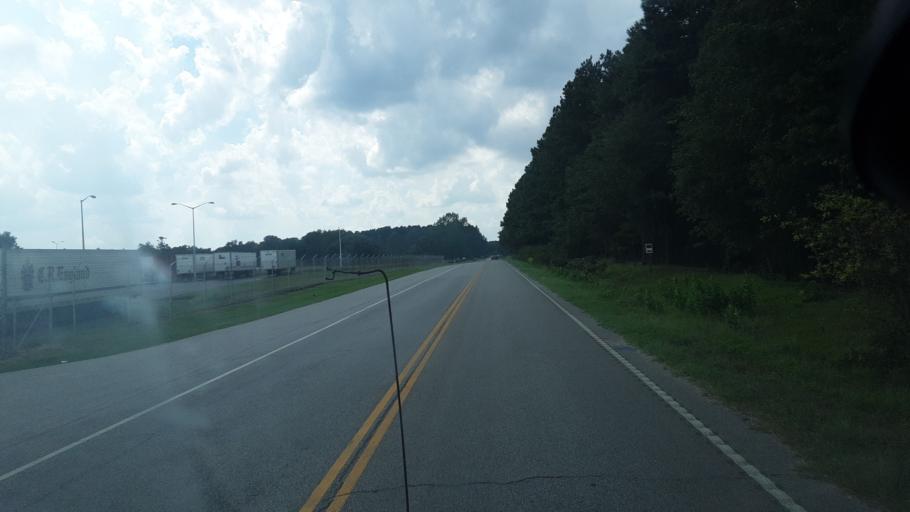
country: US
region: South Carolina
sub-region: Sumter County
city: Sumter
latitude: 33.9694
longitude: -80.3485
